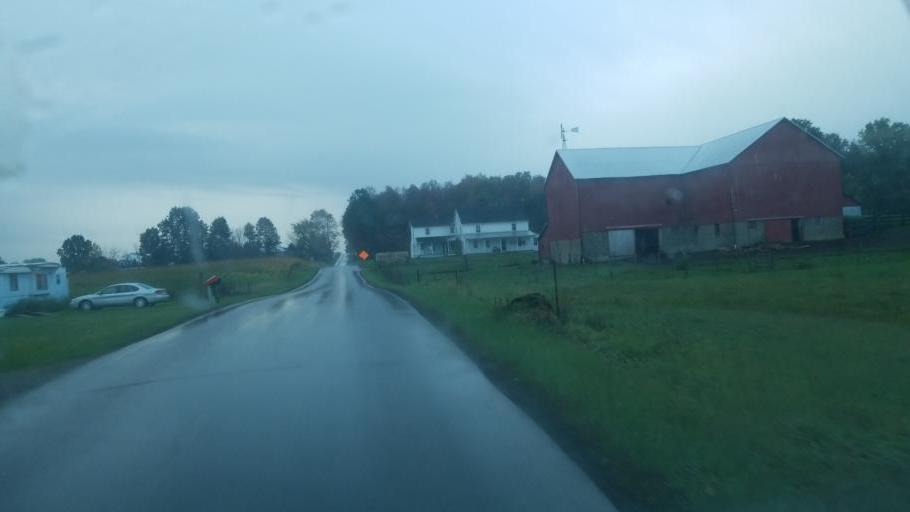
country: US
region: Ohio
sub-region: Wayne County
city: Apple Creek
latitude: 40.7216
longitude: -81.7844
